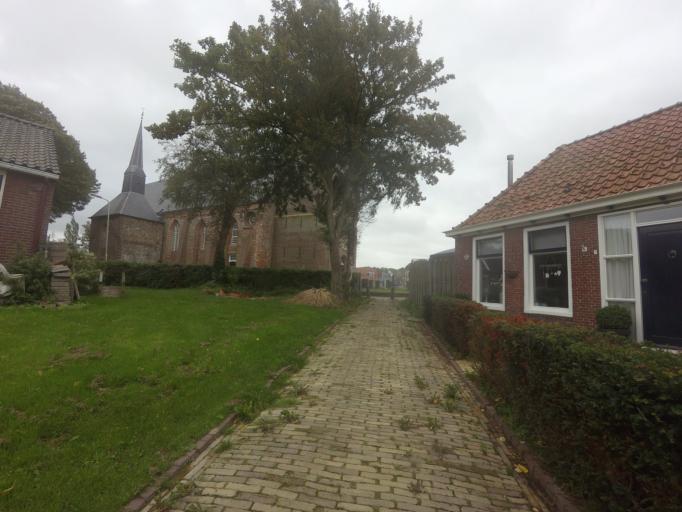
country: NL
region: Friesland
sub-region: Gemeente Ferwerderadiel
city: Hallum
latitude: 53.3075
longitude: 5.7849
